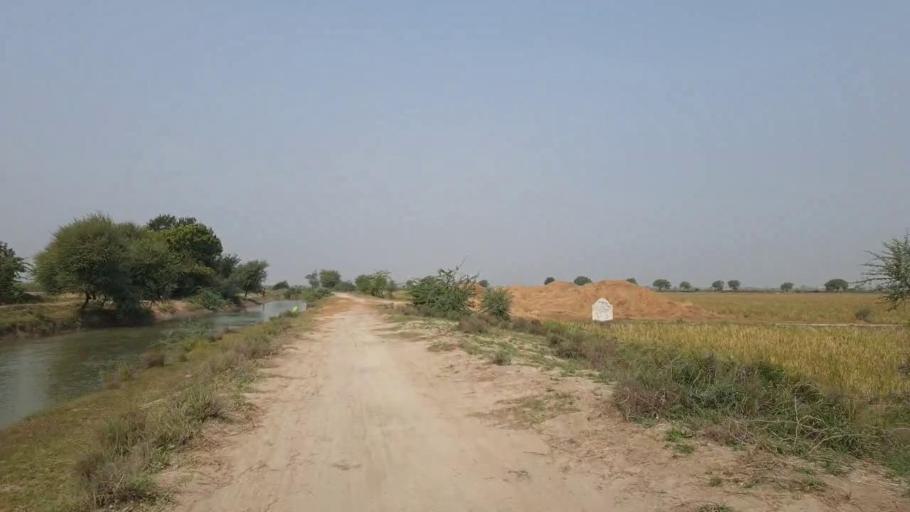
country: PK
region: Sindh
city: Kario
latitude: 24.8447
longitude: 68.5365
